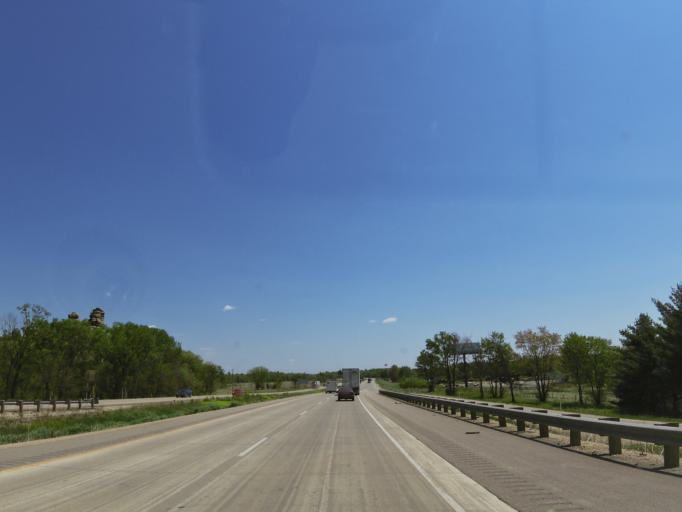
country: US
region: Wisconsin
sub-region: Juneau County
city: New Lisbon
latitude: 43.9214
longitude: -90.2619
